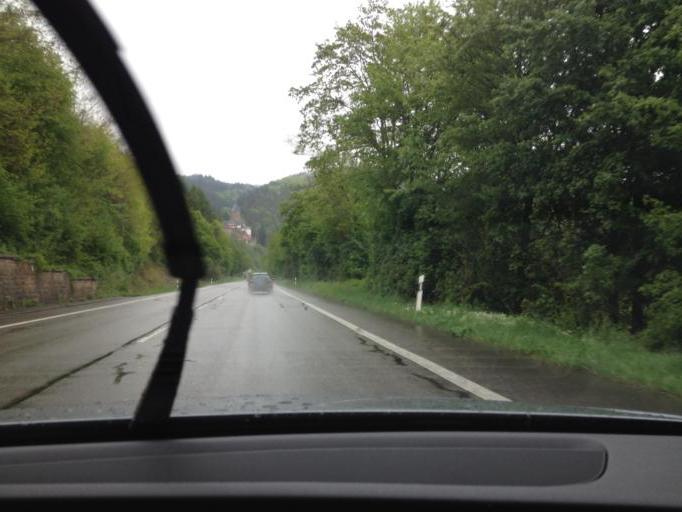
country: DE
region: Baden-Wuerttemberg
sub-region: Karlsruhe Region
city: Zwingenberg
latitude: 49.4178
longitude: 9.0218
